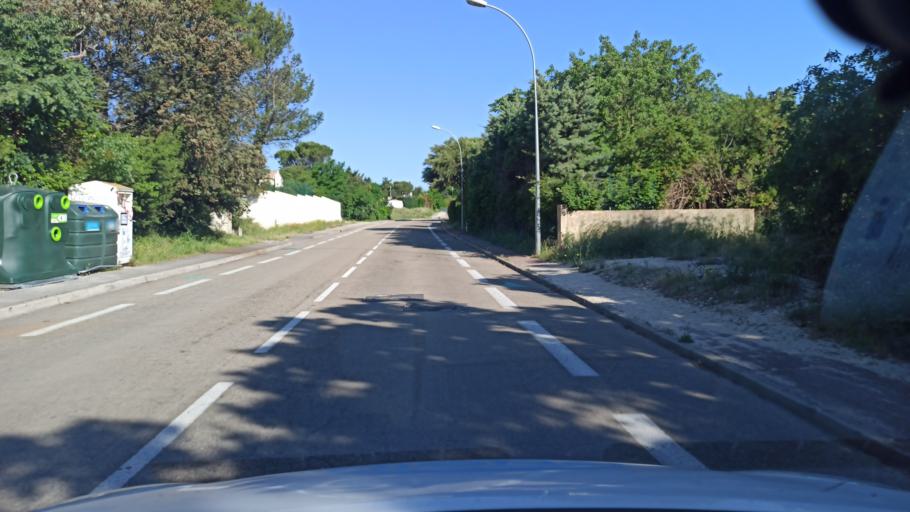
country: FR
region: Languedoc-Roussillon
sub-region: Departement du Gard
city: Les Angles
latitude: 43.9753
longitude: 4.7747
